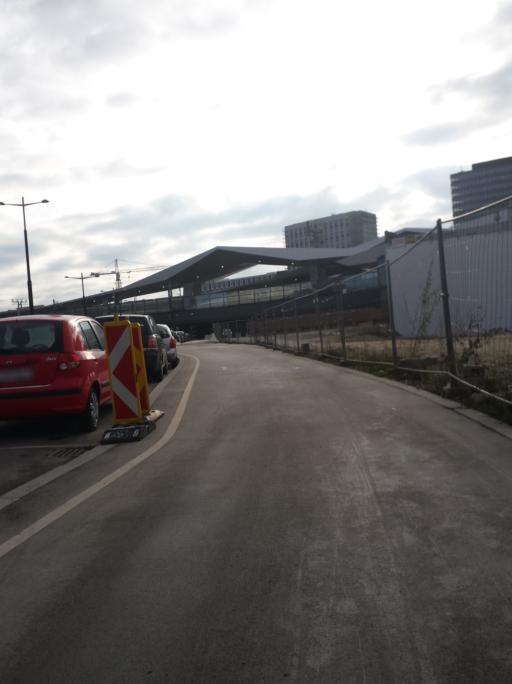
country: AT
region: Vienna
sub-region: Wien Stadt
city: Vienna
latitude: 48.1867
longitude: 16.3775
